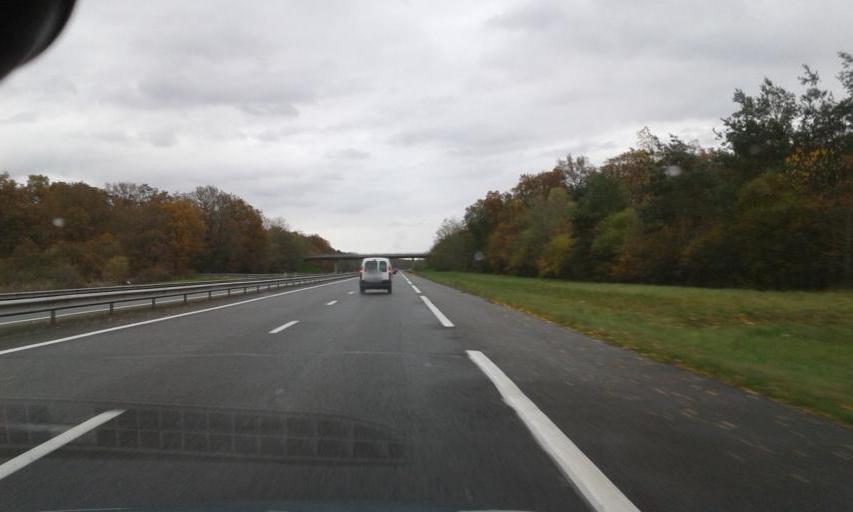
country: FR
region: Centre
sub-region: Departement du Loiret
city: Fay-aux-Loges
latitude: 47.9085
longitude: 2.1701
